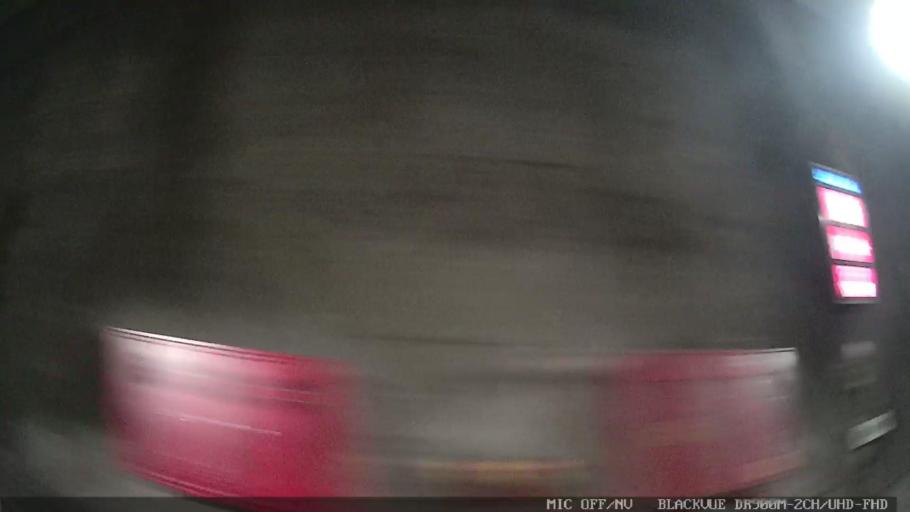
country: BR
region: Sao Paulo
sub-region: Cubatao
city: Cubatao
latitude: -23.8800
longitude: -46.4846
